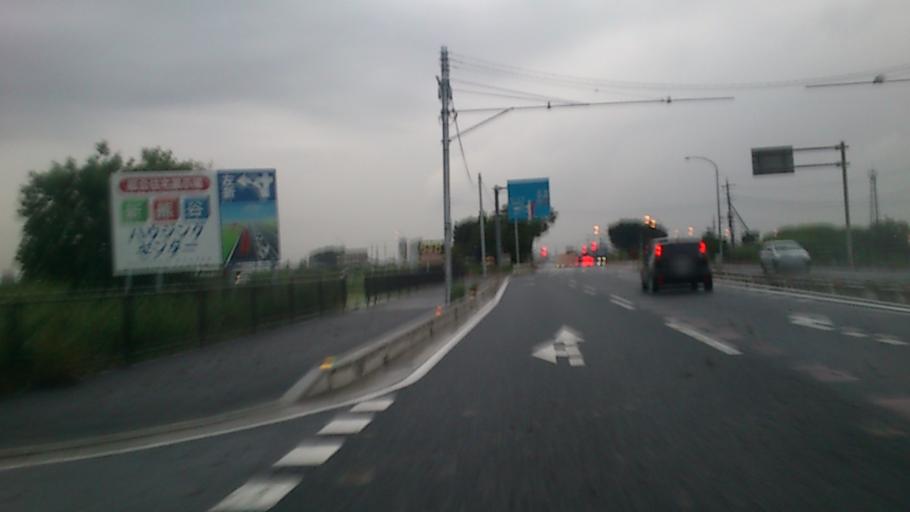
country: JP
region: Saitama
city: Kumagaya
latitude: 36.1517
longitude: 139.4226
